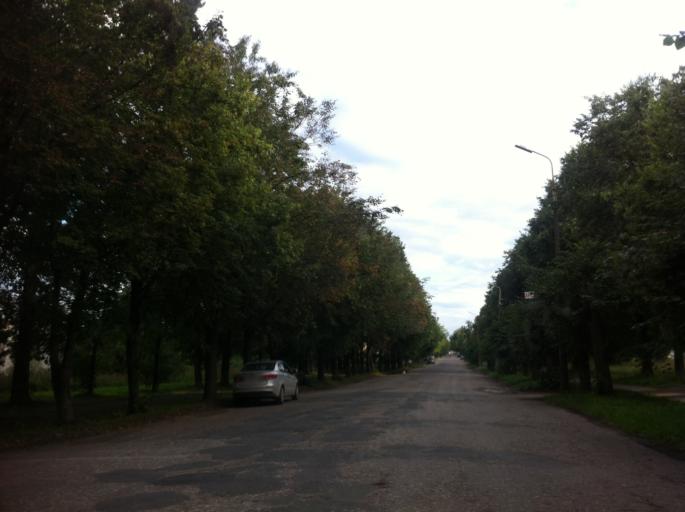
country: RU
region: Pskov
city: Pskov
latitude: 57.8253
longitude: 28.3191
